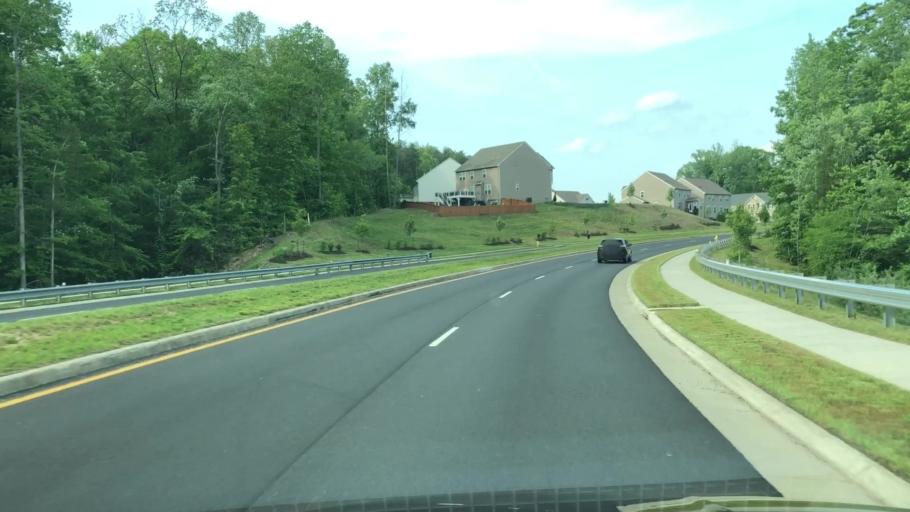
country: US
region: Virginia
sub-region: Stafford County
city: Stafford
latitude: 38.4319
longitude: -77.4604
